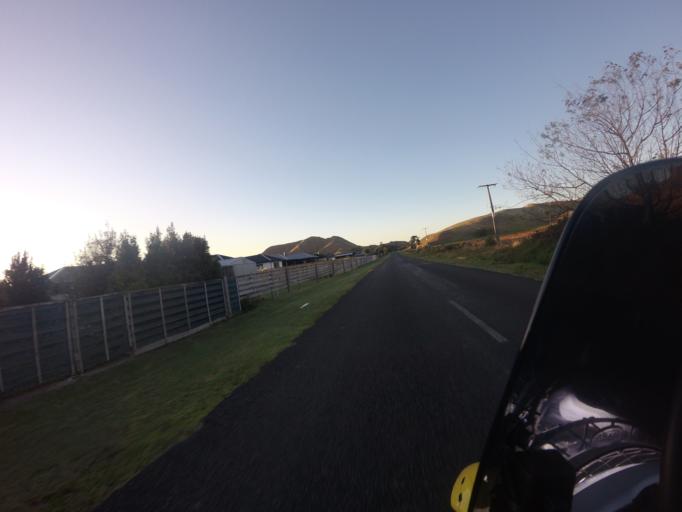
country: NZ
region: Gisborne
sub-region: Gisborne District
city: Gisborne
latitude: -38.6902
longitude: 178.0569
